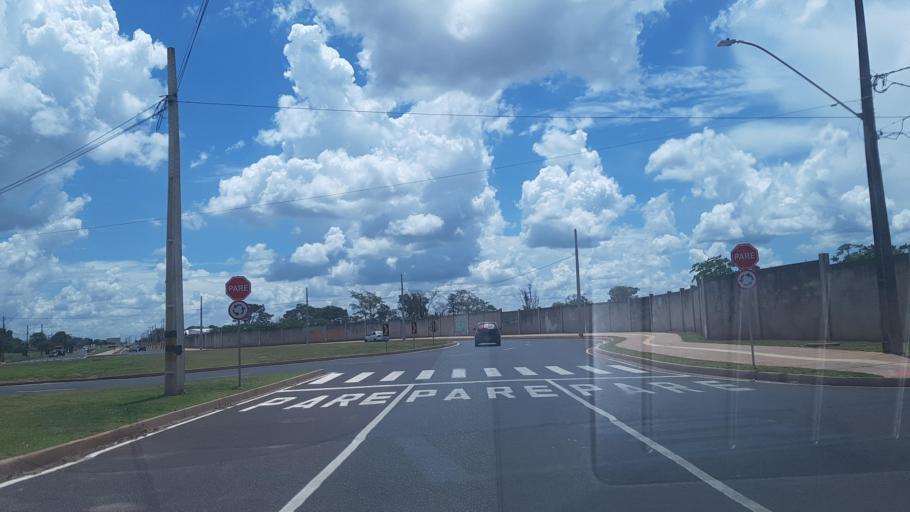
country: BR
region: Minas Gerais
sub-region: Uberlandia
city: Uberlandia
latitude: -18.9507
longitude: -48.3245
